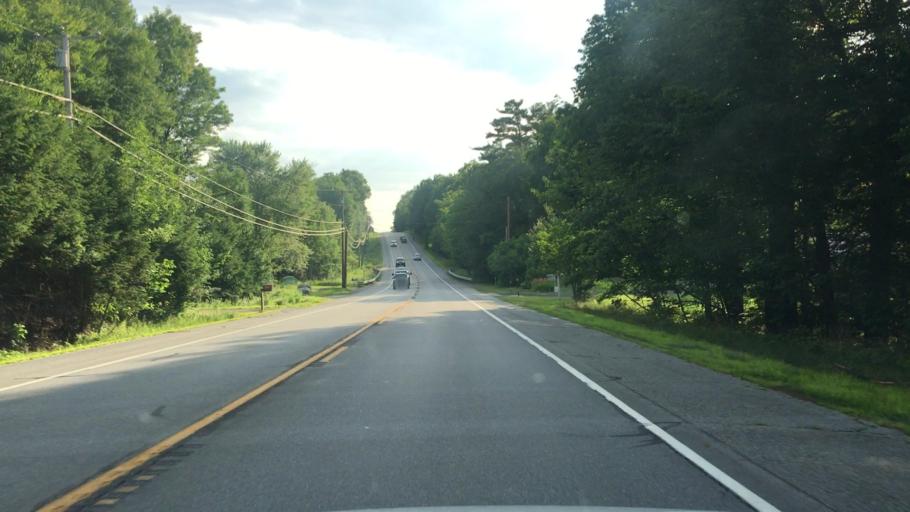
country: US
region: Maine
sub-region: Kennebec County
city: Augusta
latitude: 44.3346
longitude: -69.7017
